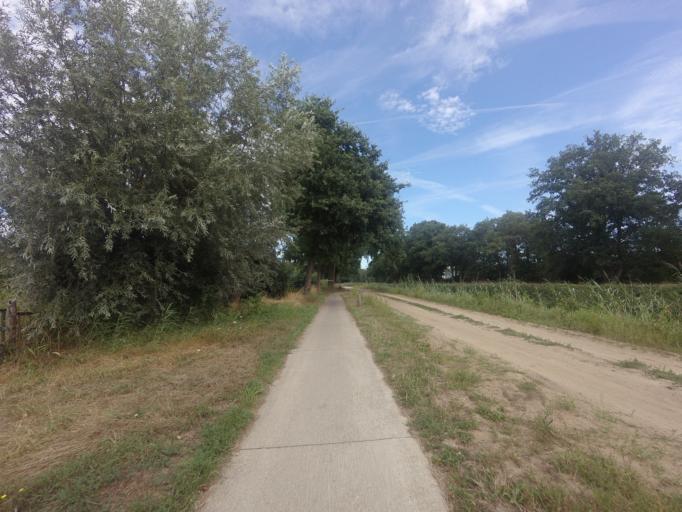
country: NL
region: Overijssel
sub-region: Gemeente Raalte
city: Raalte
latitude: 52.4249
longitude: 6.3208
